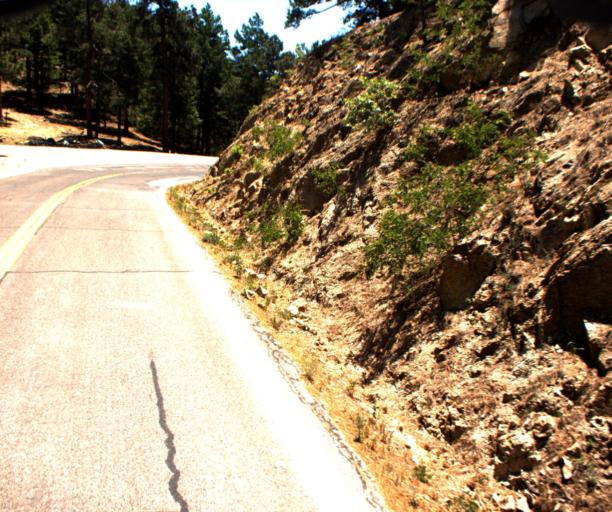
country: US
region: Arizona
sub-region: Graham County
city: Swift Trail Junction
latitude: 32.6226
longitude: -109.8241
